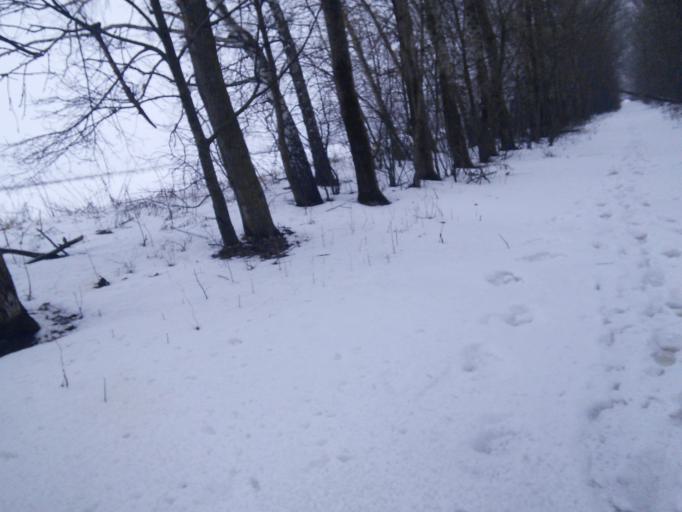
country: RU
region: Kursk
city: Chernitsyno
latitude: 51.5739
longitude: 36.0855
